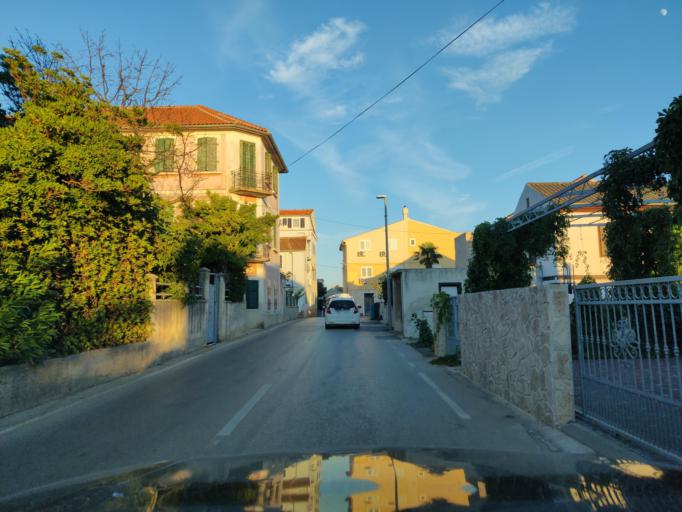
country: HR
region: Sibensko-Kniniska
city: Murter
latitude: 43.8236
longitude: 15.6028
